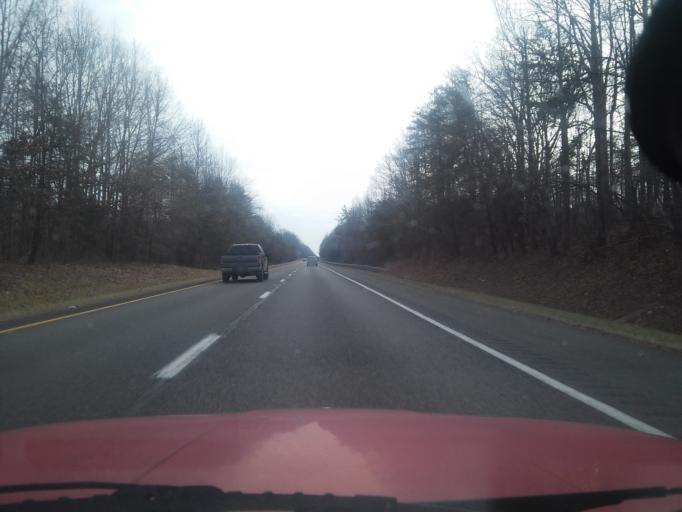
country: US
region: Virginia
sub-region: Louisa County
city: Louisa
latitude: 37.8668
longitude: -78.0093
